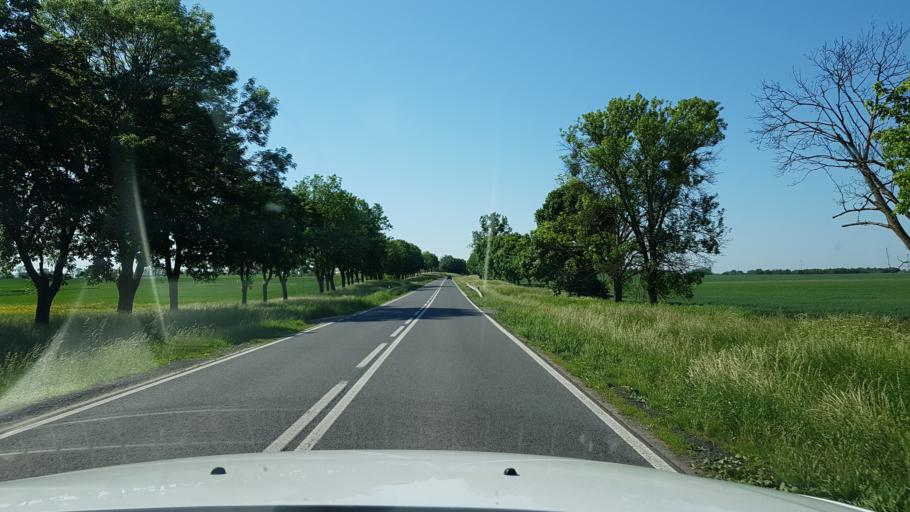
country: PL
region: West Pomeranian Voivodeship
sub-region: Powiat gryfinski
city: Mieszkowice
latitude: 52.8071
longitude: 14.4985
